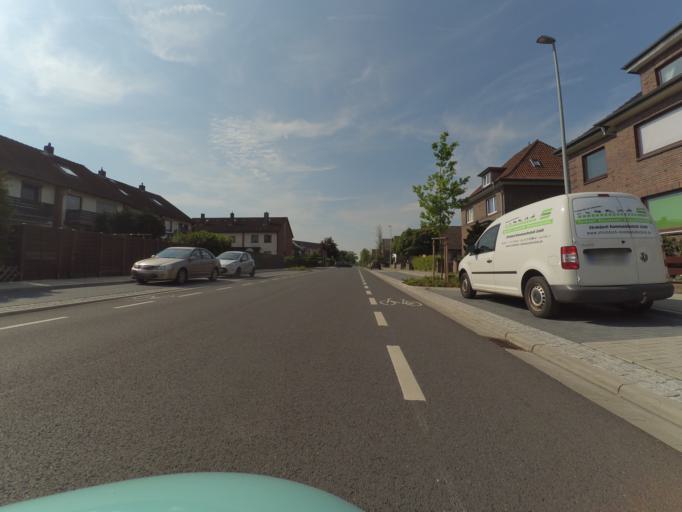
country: DE
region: Lower Saxony
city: Lehrte
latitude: 52.3820
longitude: 9.9826
